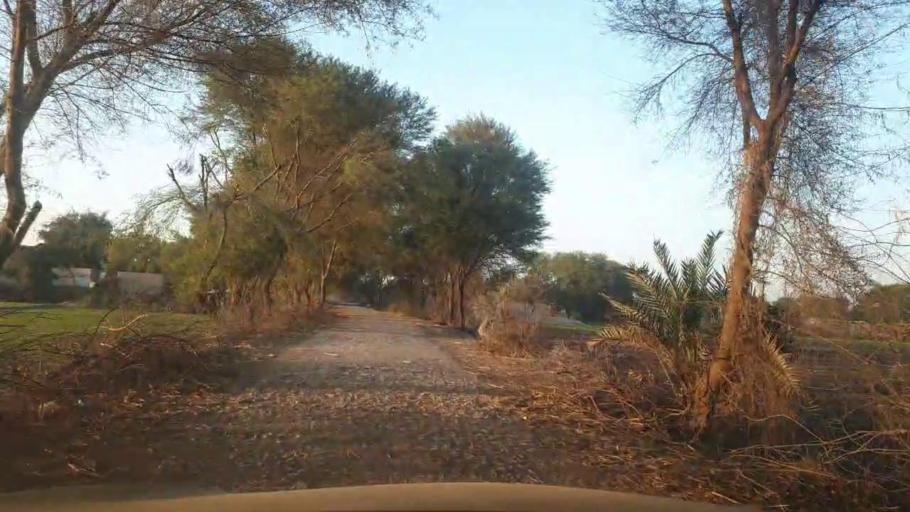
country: PK
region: Sindh
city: Ubauro
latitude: 28.1863
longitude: 69.6021
